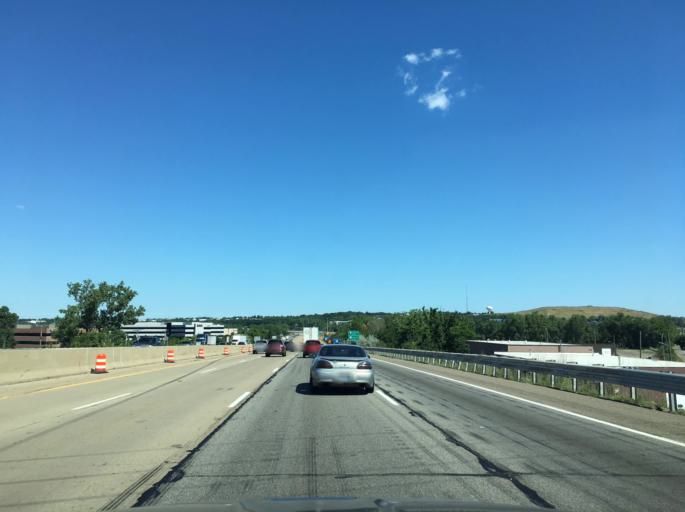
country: US
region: Michigan
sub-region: Oakland County
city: Auburn Hills
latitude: 42.6844
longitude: -83.2441
